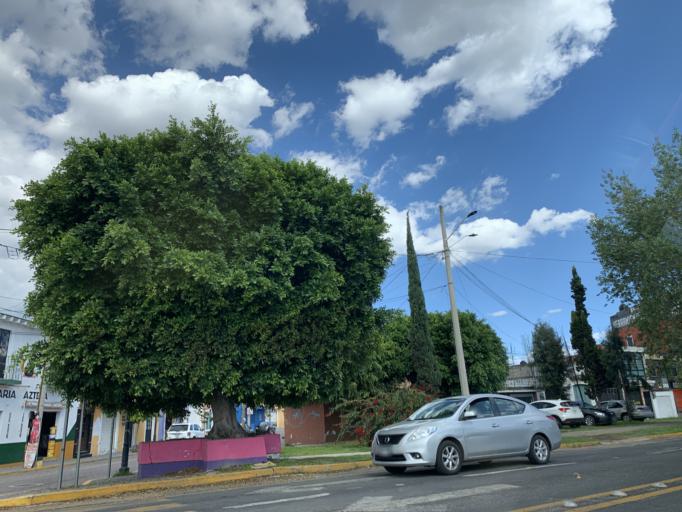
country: MX
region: Puebla
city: Cholula
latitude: 19.0673
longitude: -98.3148
